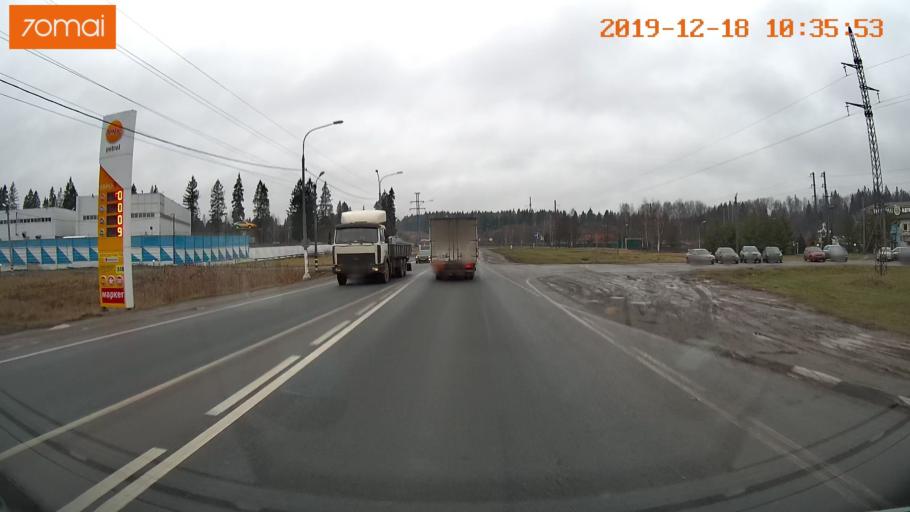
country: RU
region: Moskovskaya
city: Troitsk
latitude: 55.4164
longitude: 37.1919
